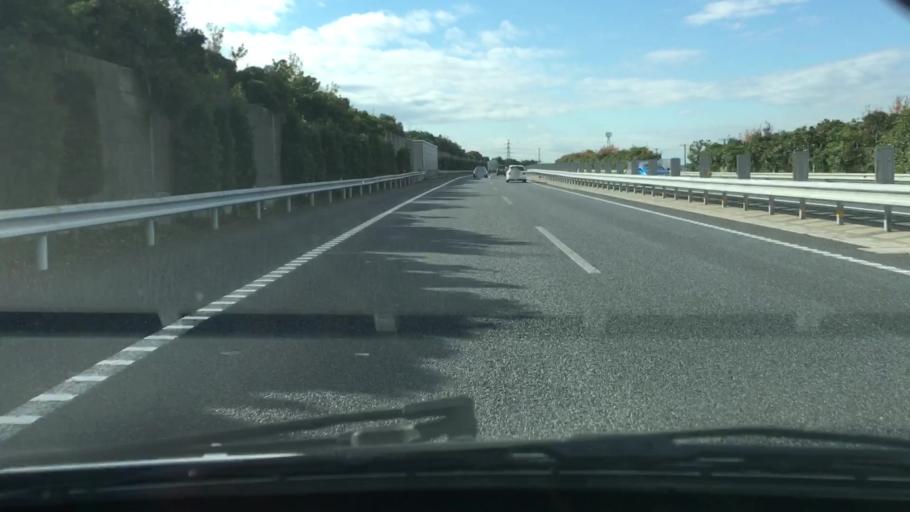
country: JP
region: Chiba
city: Ichihara
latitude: 35.5174
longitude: 140.1198
